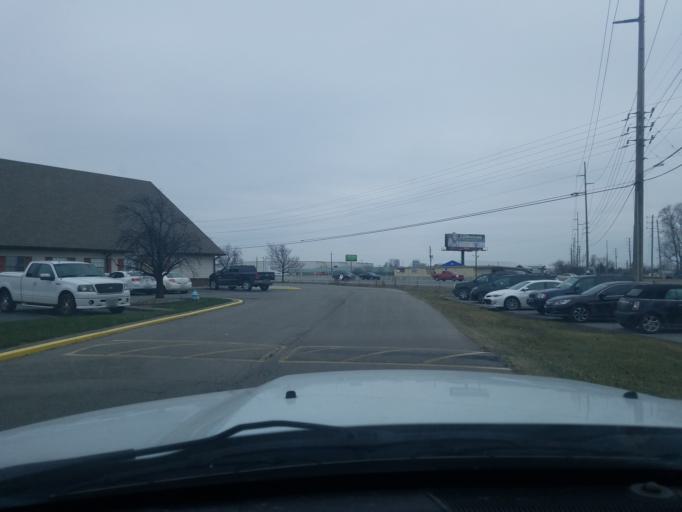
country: US
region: Indiana
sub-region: Hamilton County
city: Fishers
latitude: 39.9124
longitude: -86.0394
